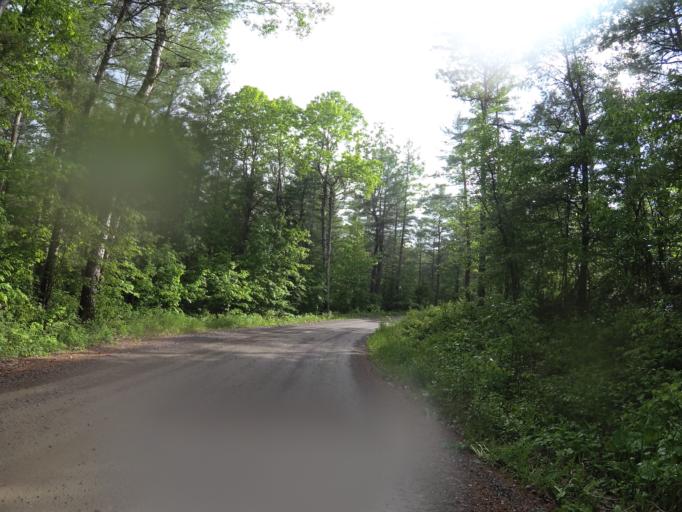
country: CA
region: Ontario
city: Renfrew
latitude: 45.1815
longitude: -76.9158
